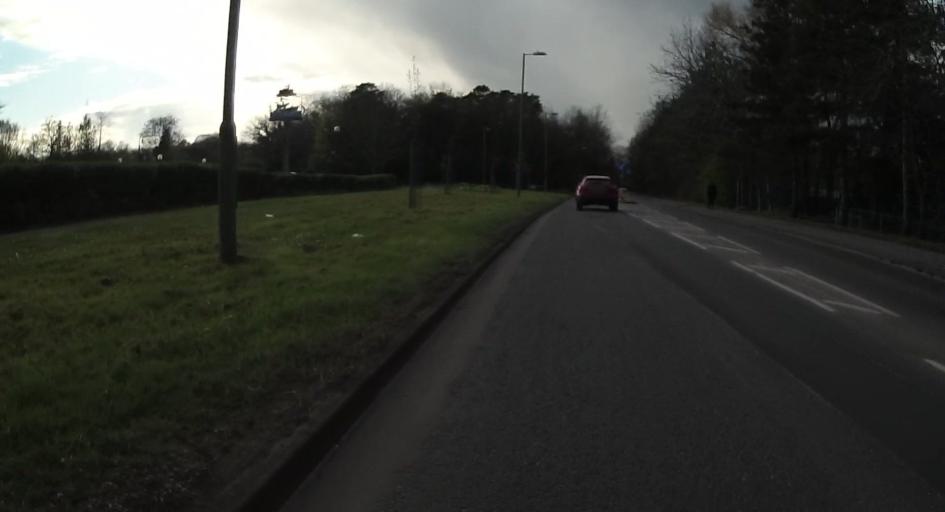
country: GB
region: England
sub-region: Hampshire
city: Fleet
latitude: 51.2925
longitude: -0.8279
